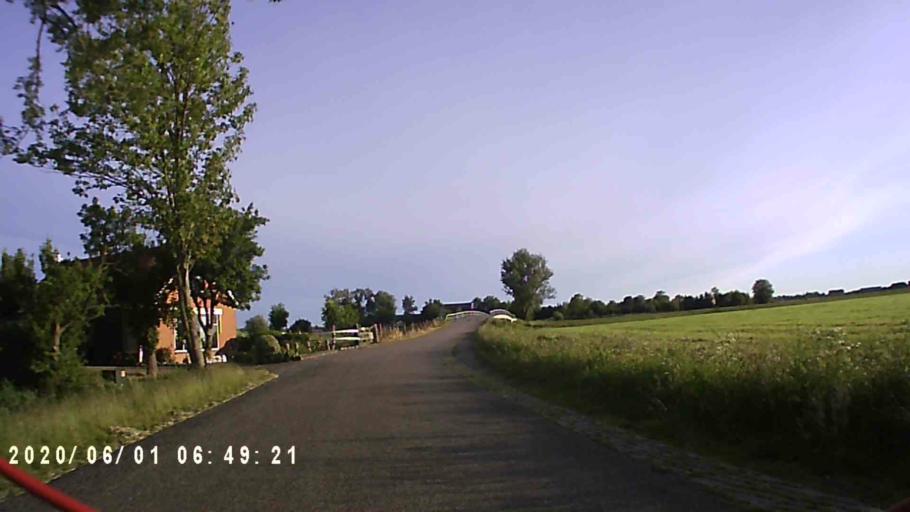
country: NL
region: Friesland
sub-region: Gemeente Kollumerland en Nieuwkruisland
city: Kollum
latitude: 53.2989
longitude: 6.1312
